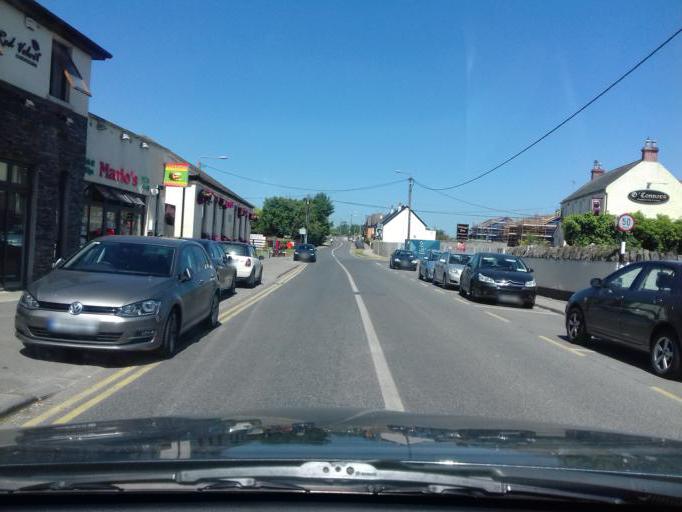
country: IE
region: Leinster
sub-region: Fingal County
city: Swords
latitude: 53.5216
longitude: -6.2675
